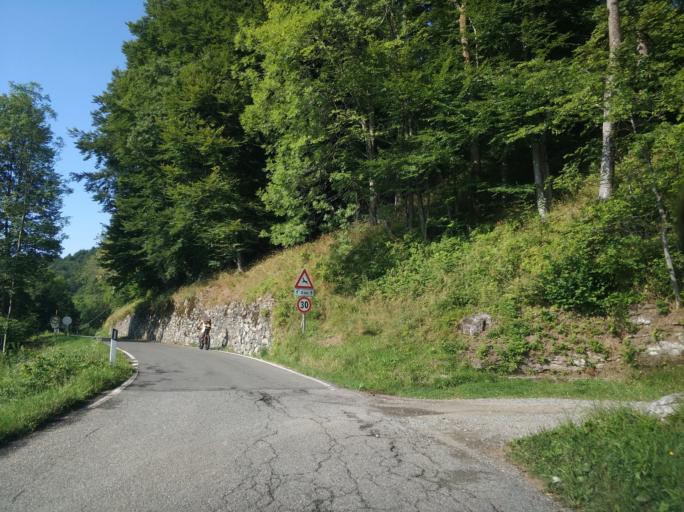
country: IT
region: Piedmont
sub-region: Provincia di Torino
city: Viu
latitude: 45.2138
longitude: 7.3758
